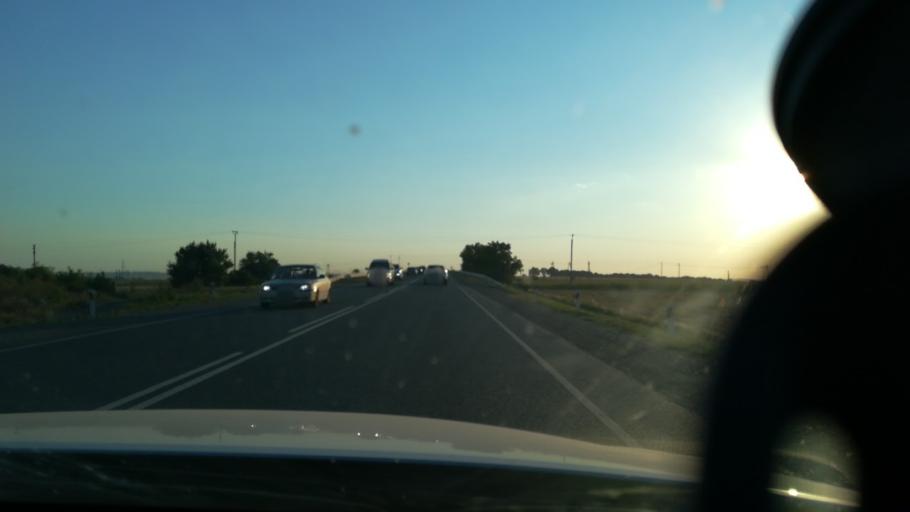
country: RU
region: Krasnodarskiy
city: Yurovka
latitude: 45.1188
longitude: 37.3929
